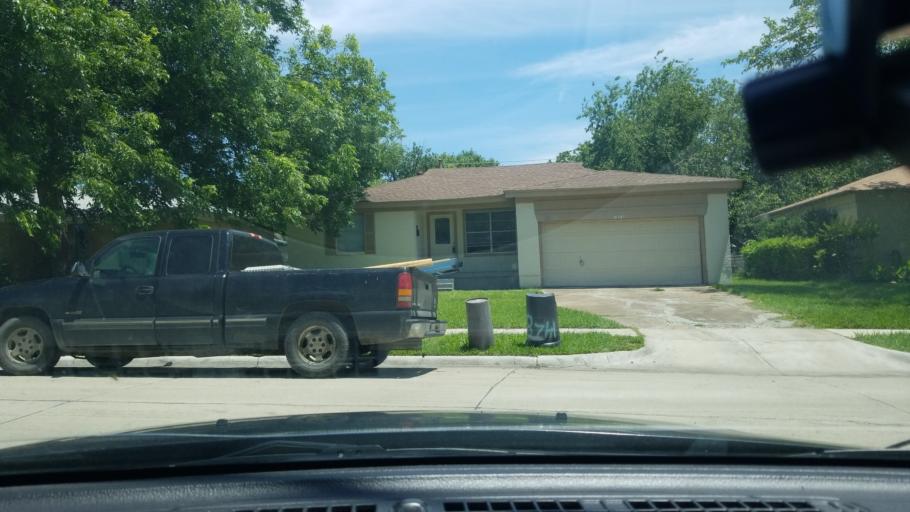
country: US
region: Texas
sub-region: Dallas County
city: Mesquite
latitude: 32.7874
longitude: -96.6178
